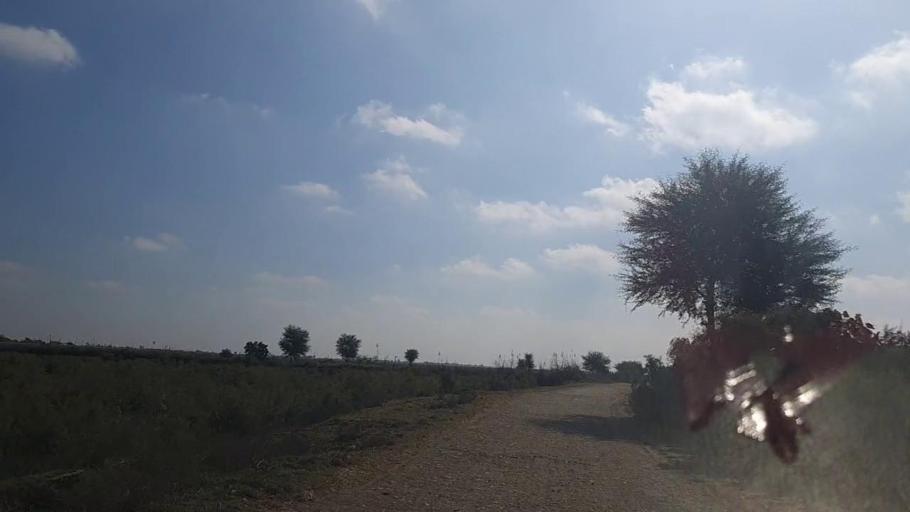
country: PK
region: Sindh
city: Sanghar
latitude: 26.0614
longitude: 69.0054
